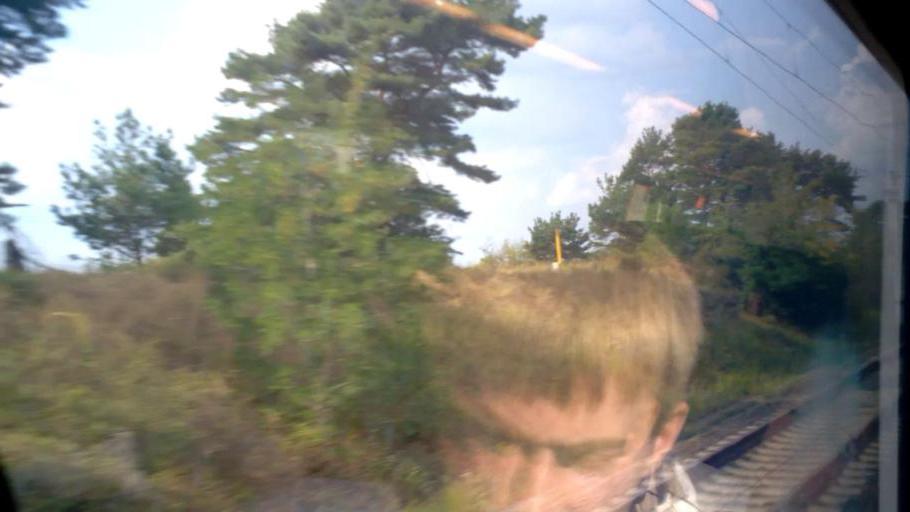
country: DE
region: Brandenburg
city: Grossbeeren
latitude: 52.3558
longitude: 13.2867
